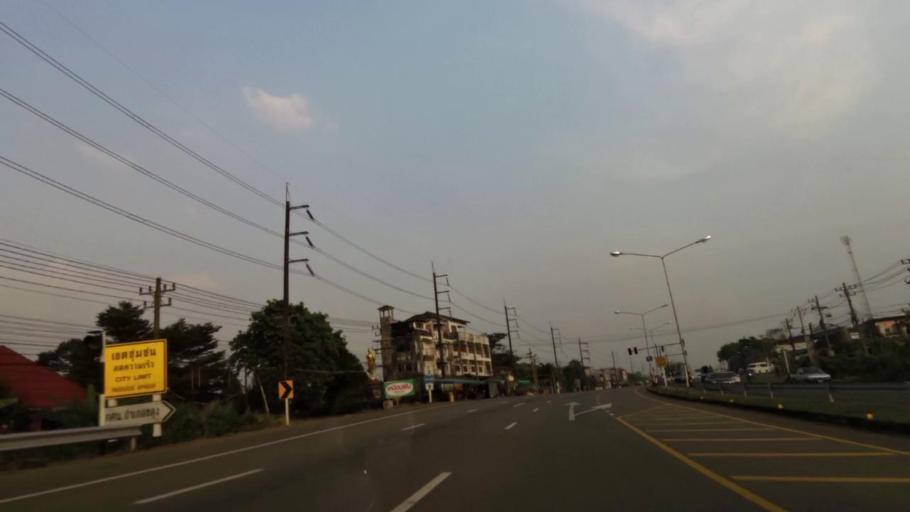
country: TH
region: Chanthaburi
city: Khlung
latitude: 12.4657
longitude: 102.2213
